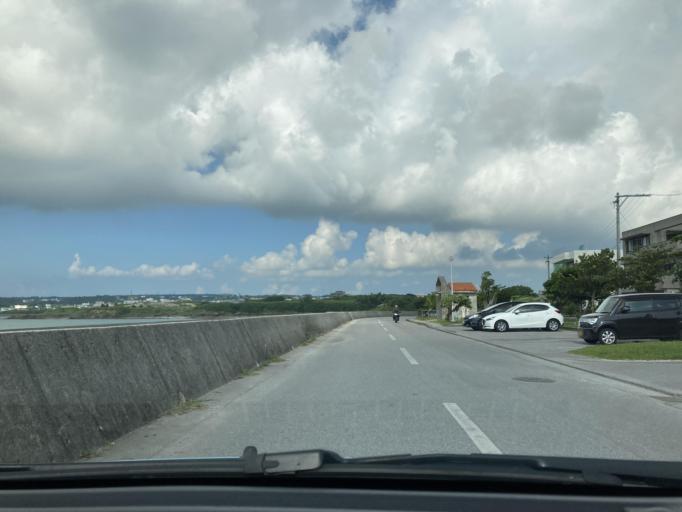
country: JP
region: Okinawa
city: Itoman
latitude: 26.1274
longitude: 127.7725
